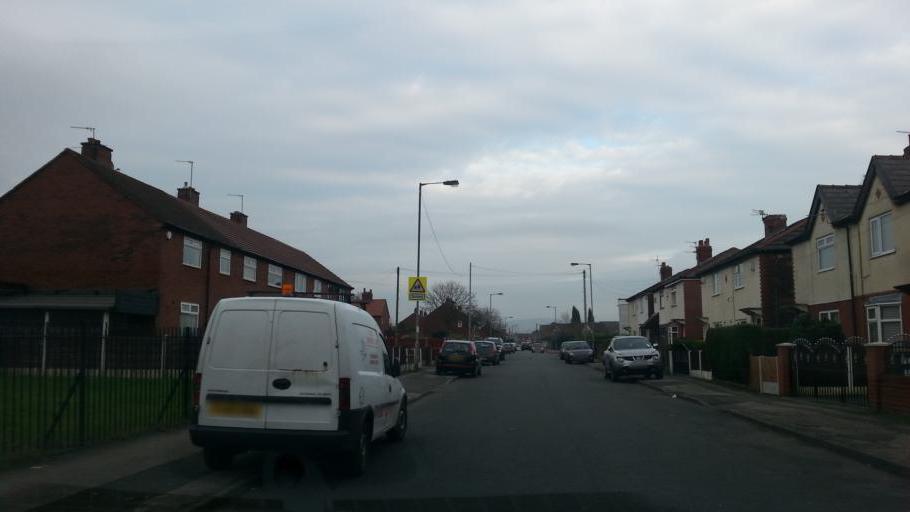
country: GB
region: England
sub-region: Borough of Tameside
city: Denton
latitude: 53.4610
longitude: -2.1244
